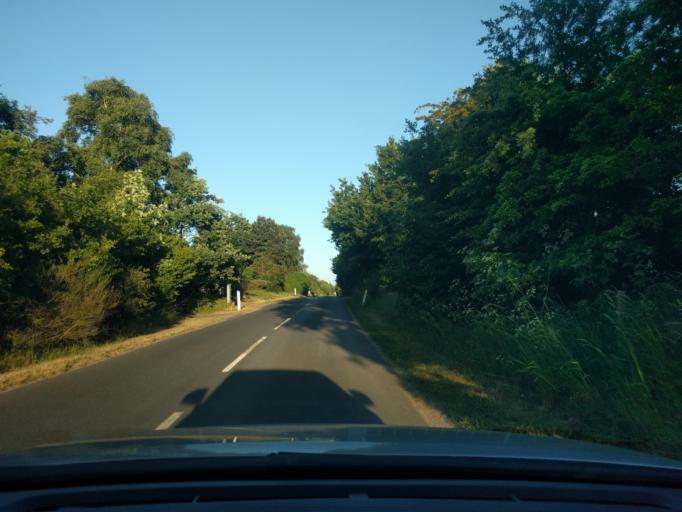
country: DK
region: South Denmark
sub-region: Kerteminde Kommune
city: Munkebo
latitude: 55.6083
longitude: 10.6174
